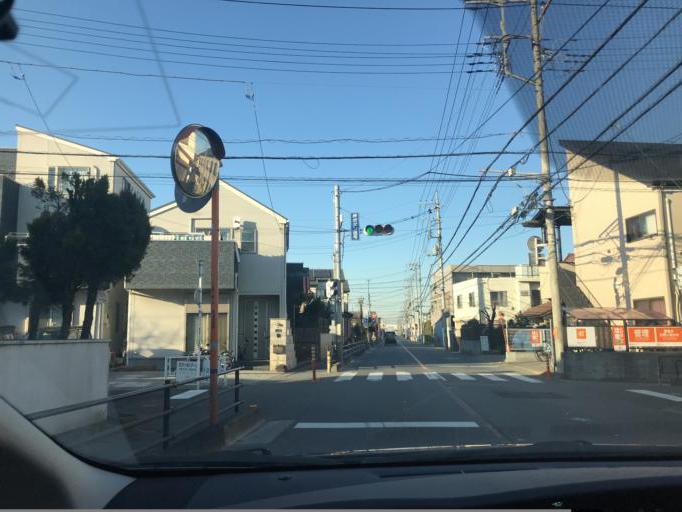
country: JP
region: Saitama
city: Yashio-shi
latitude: 35.8348
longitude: 139.8361
